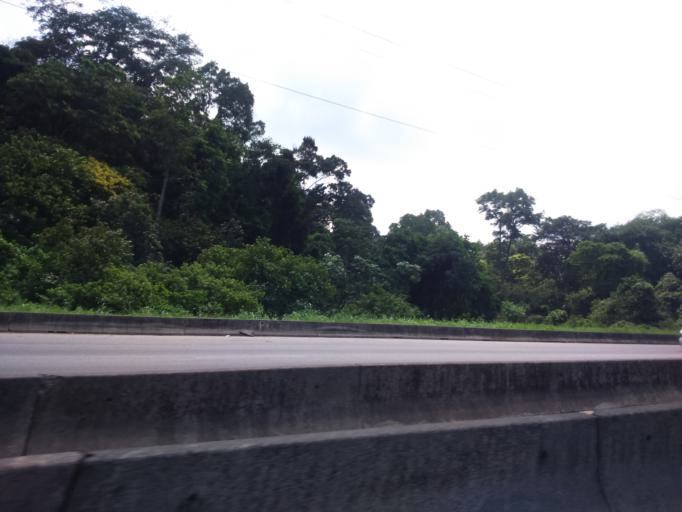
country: CI
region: Lagunes
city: Abobo
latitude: 5.3627
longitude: -4.0352
